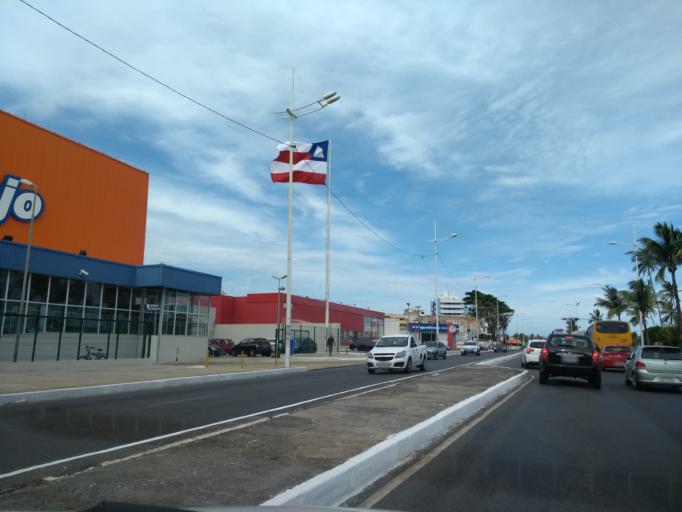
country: BR
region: Bahia
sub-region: Lauro De Freitas
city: Lauro de Freitas
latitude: -12.9531
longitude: -38.3786
